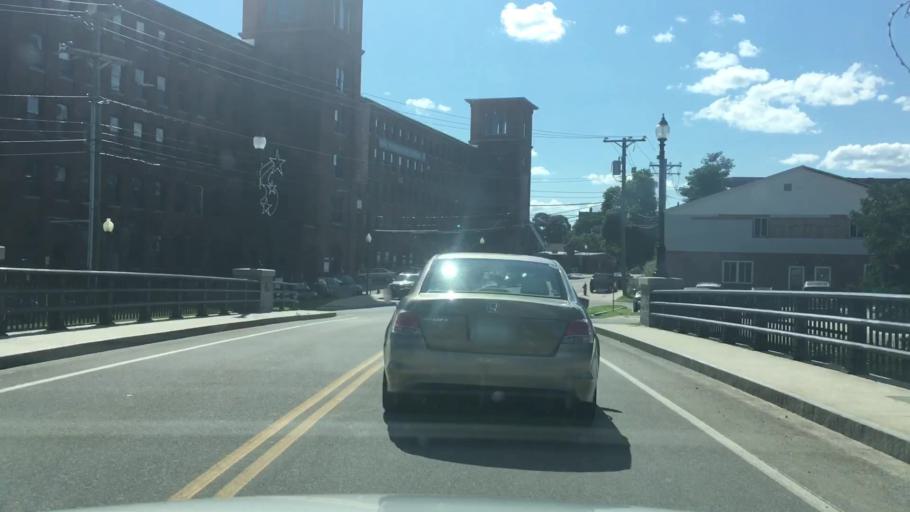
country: US
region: New Hampshire
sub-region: Strafford County
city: Dover
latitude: 43.1953
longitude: -70.8701
